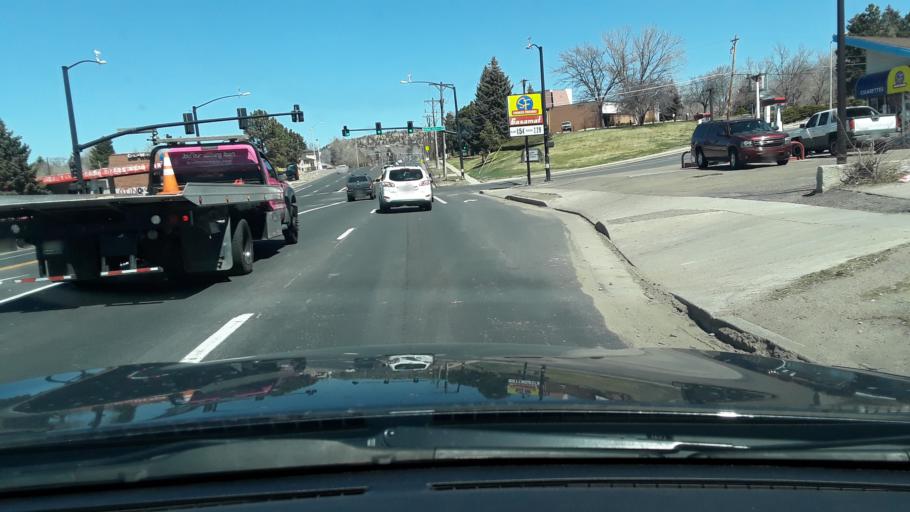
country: US
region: Colorado
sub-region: El Paso County
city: Colorado Springs
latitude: 38.8537
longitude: -104.7757
